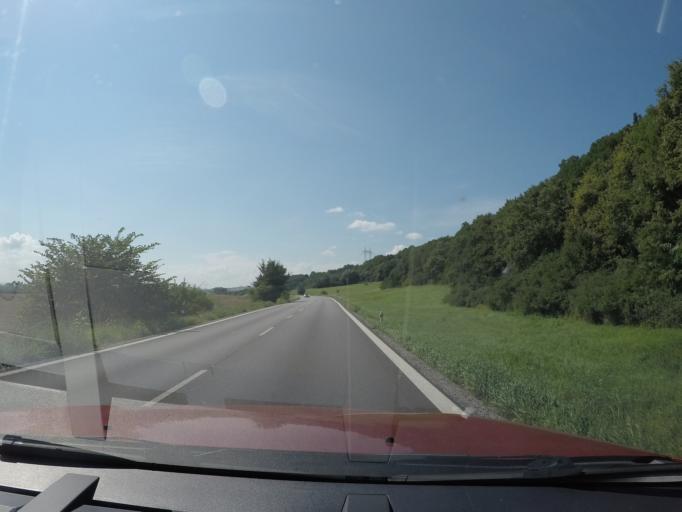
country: SK
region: Presovsky
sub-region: Okres Presov
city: Presov
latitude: 48.8910
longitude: 21.2443
